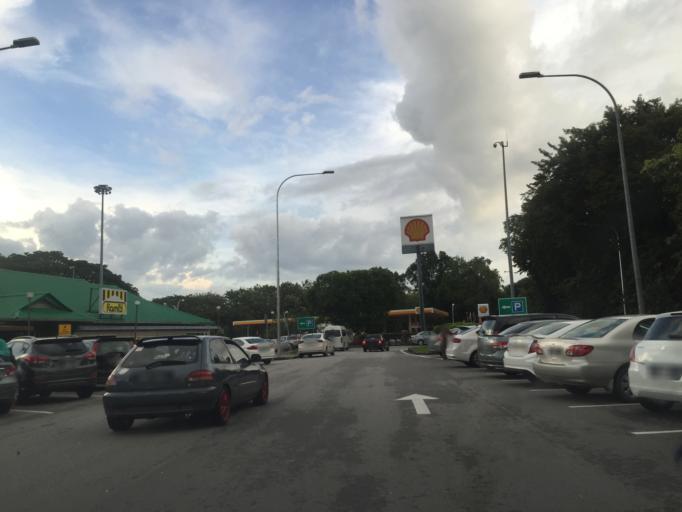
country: MY
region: Kedah
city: Gurun
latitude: 5.8309
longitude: 100.4889
